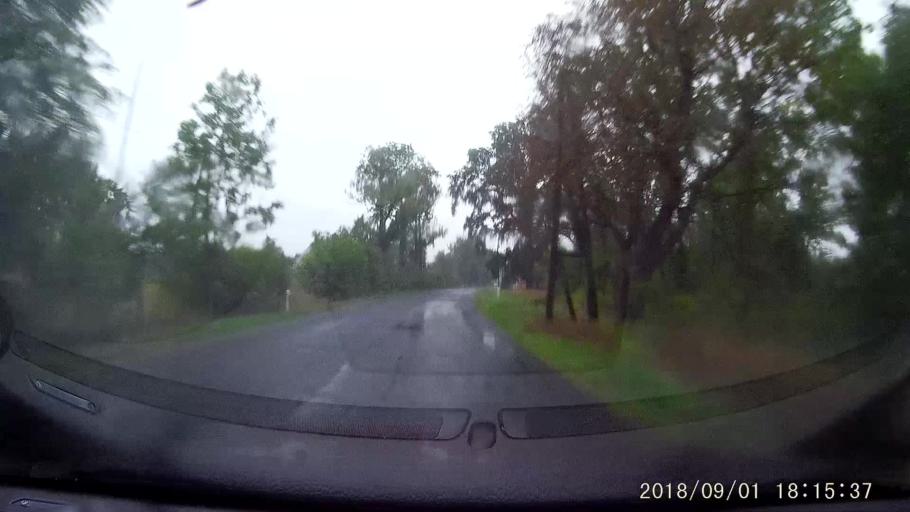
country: PL
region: Lower Silesian Voivodeship
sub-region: Powiat zgorzelecki
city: Piensk
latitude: 51.2802
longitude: 15.0578
